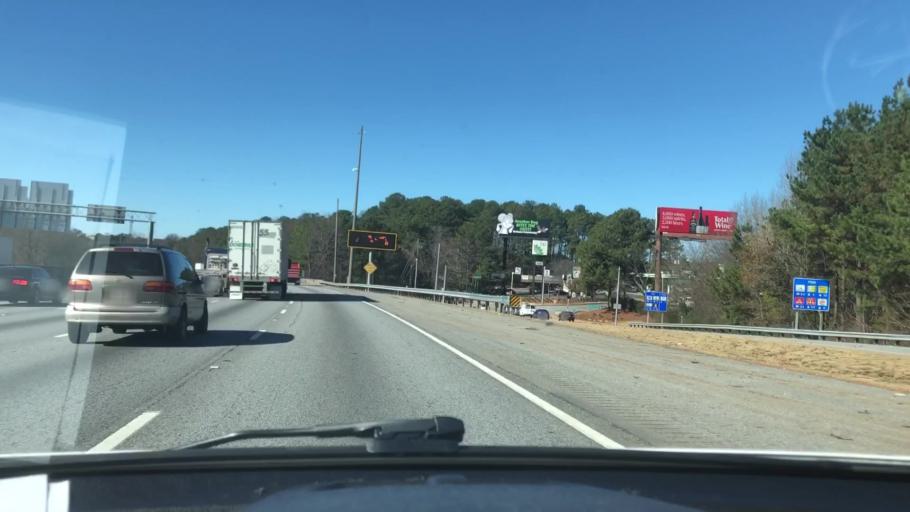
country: US
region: Georgia
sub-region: DeKalb County
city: Doraville
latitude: 33.9201
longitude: -84.2957
